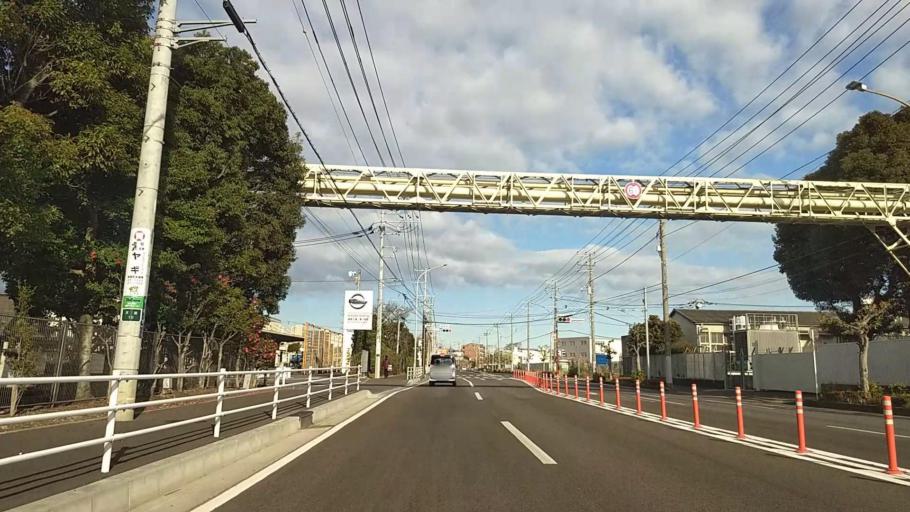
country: JP
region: Kanagawa
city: Hiratsuka
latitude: 35.3382
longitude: 139.3571
